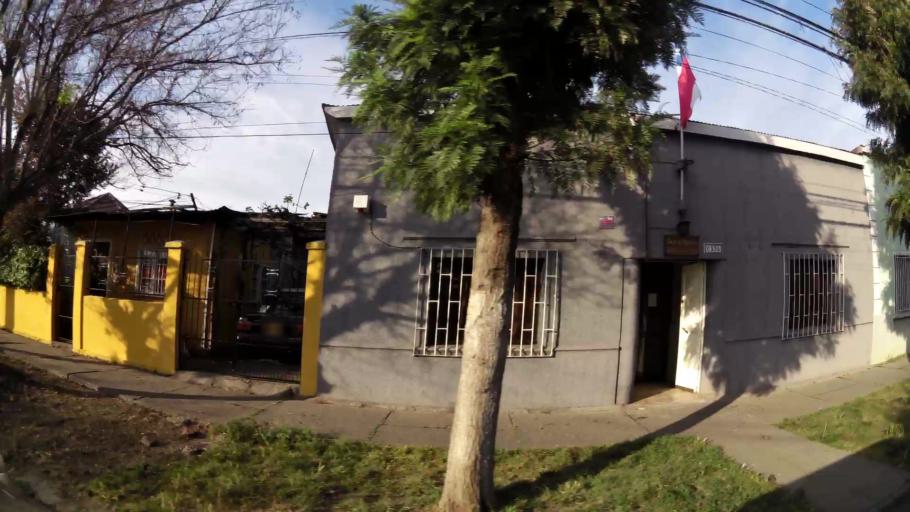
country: CL
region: Santiago Metropolitan
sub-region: Provincia de Santiago
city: La Pintana
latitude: -33.5272
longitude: -70.6677
